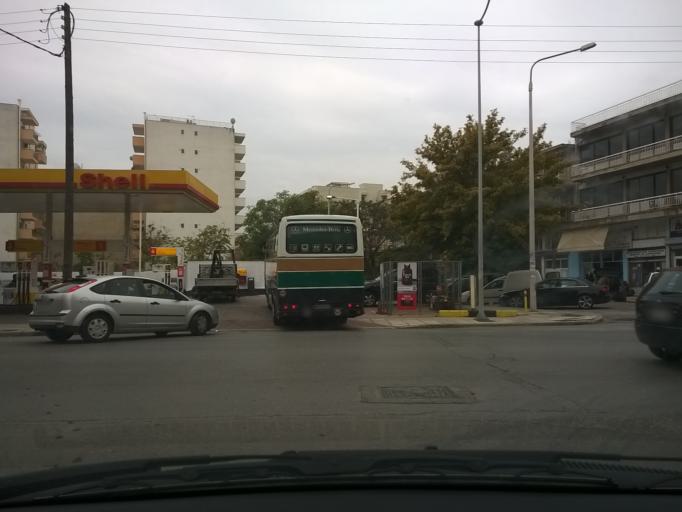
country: GR
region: Central Macedonia
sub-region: Nomos Thessalonikis
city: Thessaloniki
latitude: 40.6451
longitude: 22.9249
